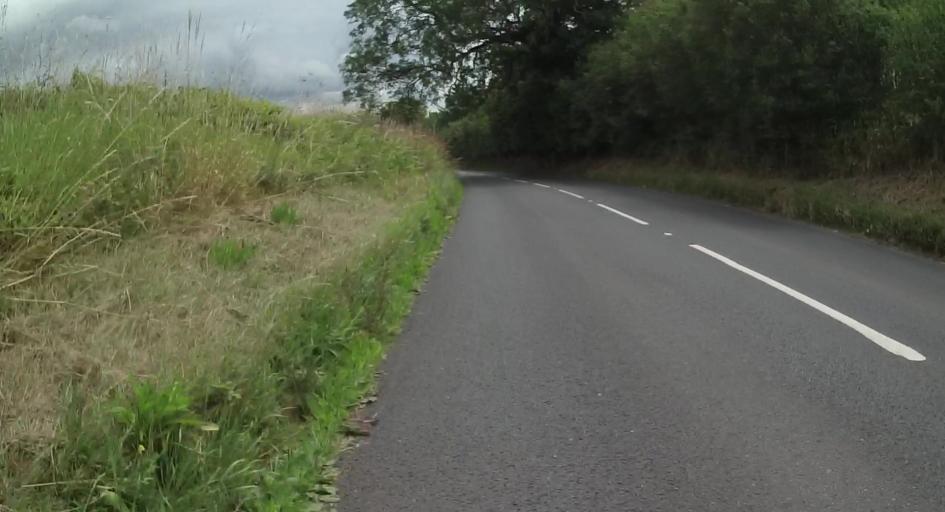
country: GB
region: England
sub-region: Surrey
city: Farnham
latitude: 51.2160
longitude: -0.8380
